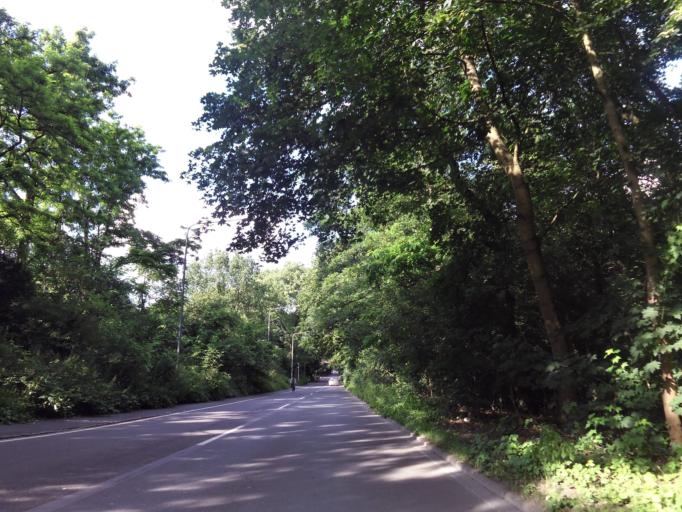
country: DE
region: Hesse
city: Niederrad
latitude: 50.0718
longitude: 8.6442
